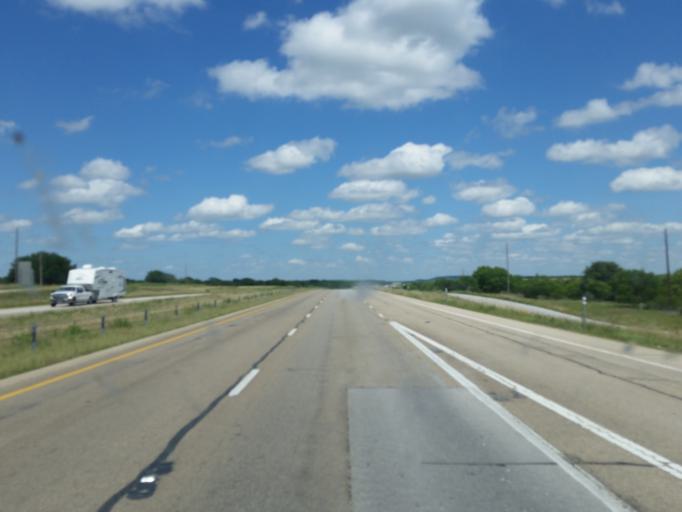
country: US
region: Texas
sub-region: Callahan County
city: Baird
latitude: 32.3854
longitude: -99.2943
